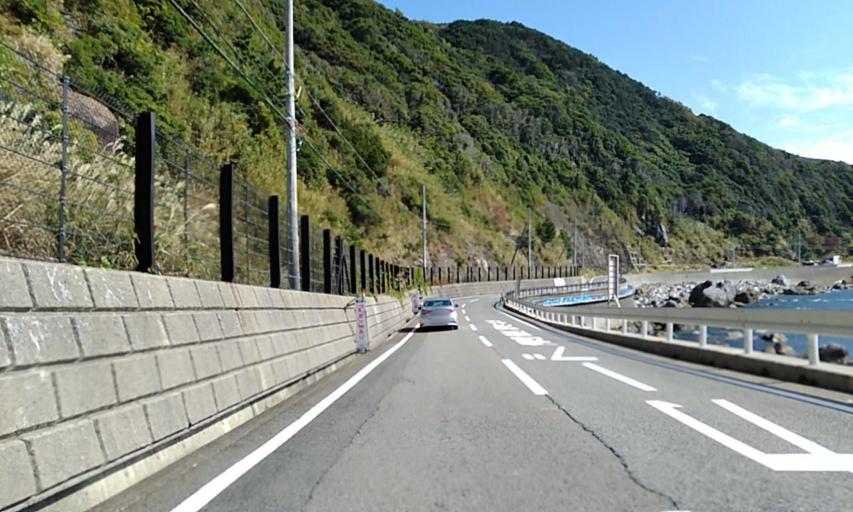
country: JP
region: Wakayama
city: Gobo
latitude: 33.9739
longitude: 135.0768
